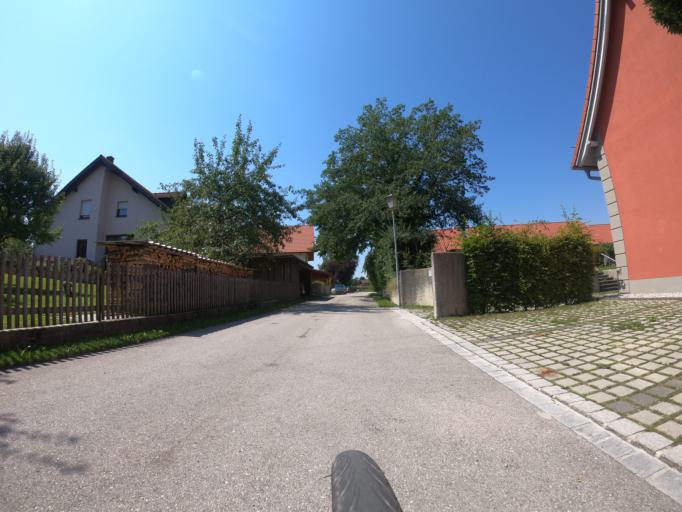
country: DE
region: Bavaria
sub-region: Upper Bavaria
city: Fuerstenfeldbruck
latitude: 48.1515
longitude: 11.2600
